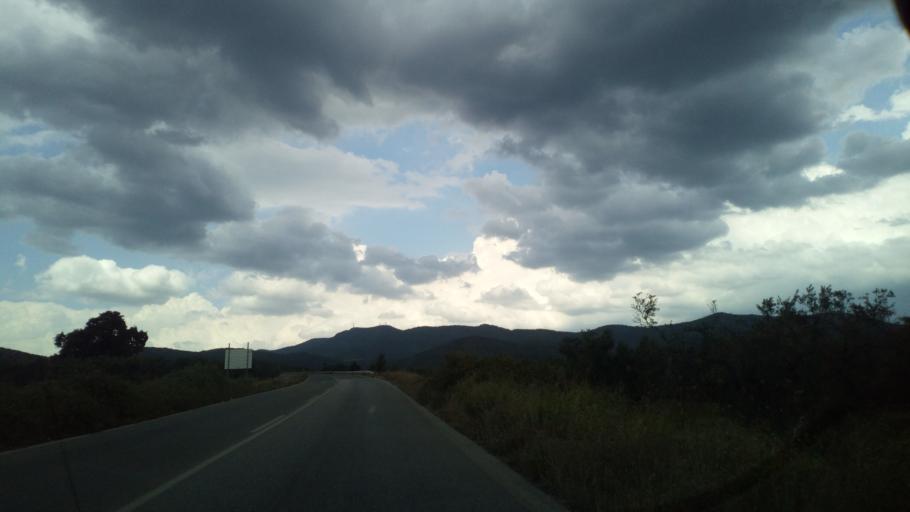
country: GR
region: Central Macedonia
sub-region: Nomos Chalkidikis
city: Polygyros
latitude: 40.3349
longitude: 23.4528
